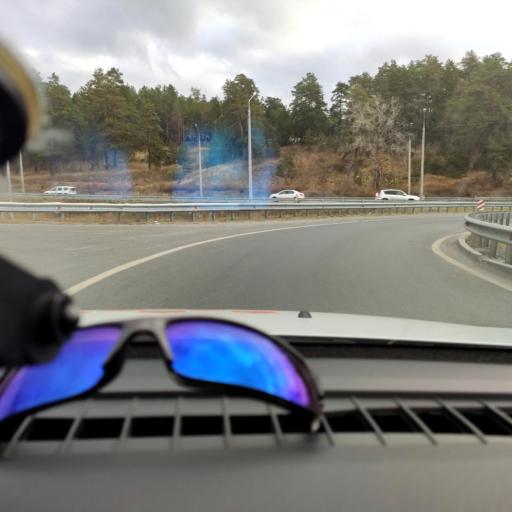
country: RU
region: Samara
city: Volzhskiy
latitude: 53.4356
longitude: 50.1123
